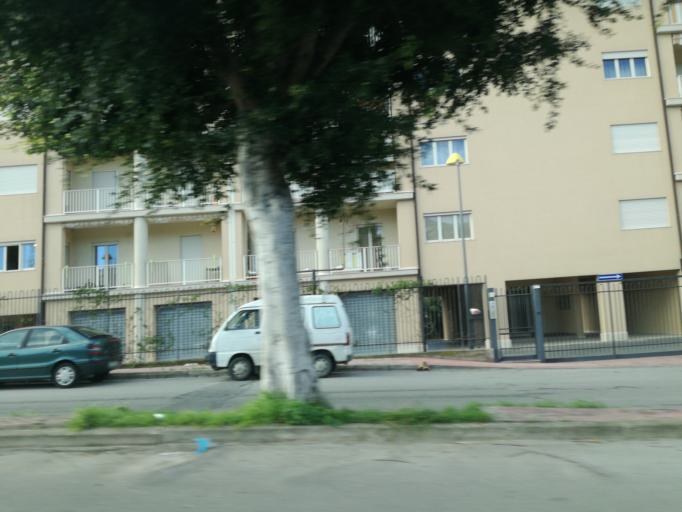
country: IT
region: Sicily
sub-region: Provincia di Caltanissetta
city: Gela
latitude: 37.0750
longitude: 14.2215
